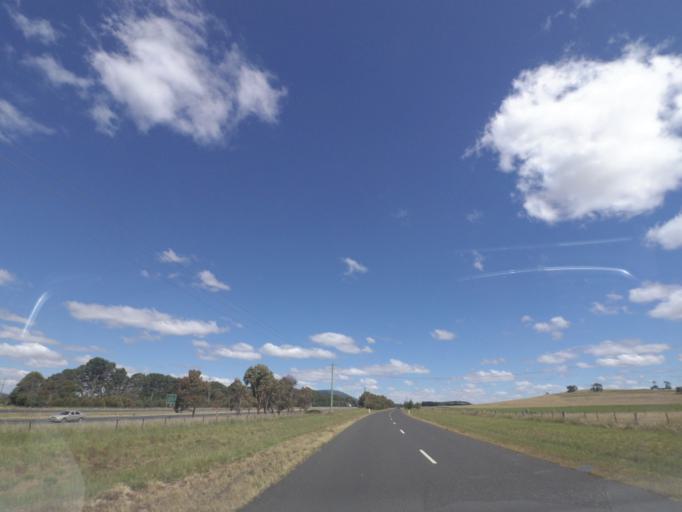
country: AU
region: Victoria
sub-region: Hume
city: Sunbury
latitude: -37.3071
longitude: 144.5156
